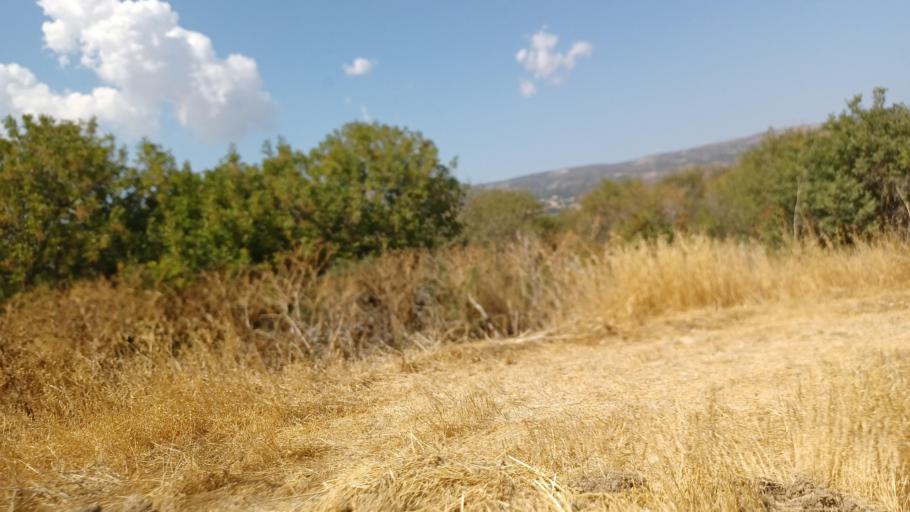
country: CY
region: Pafos
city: Polis
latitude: 34.9721
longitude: 32.4883
